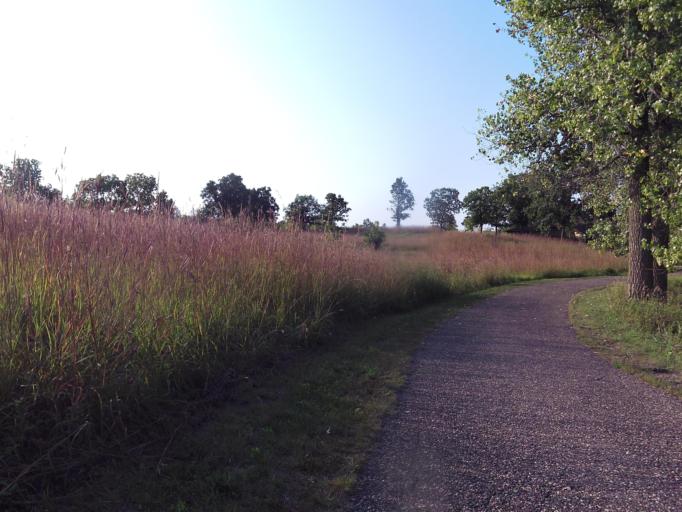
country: US
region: Minnesota
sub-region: Washington County
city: Afton
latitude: 44.8527
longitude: -92.7745
